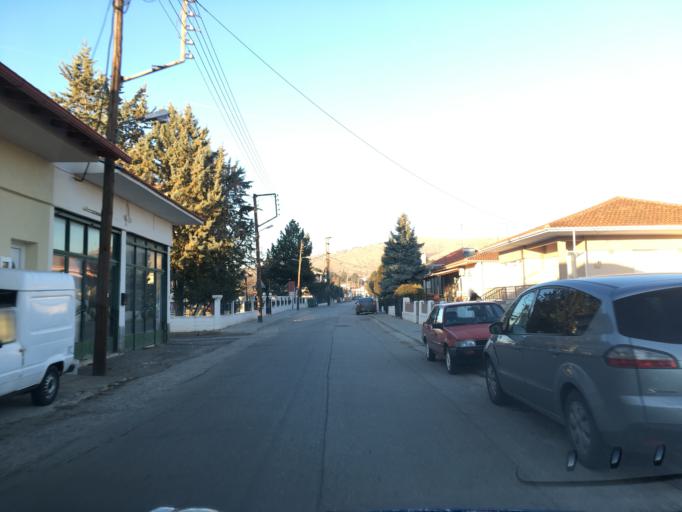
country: GR
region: West Macedonia
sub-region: Nomos Kozanis
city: Kozani
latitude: 40.2889
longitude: 21.7340
